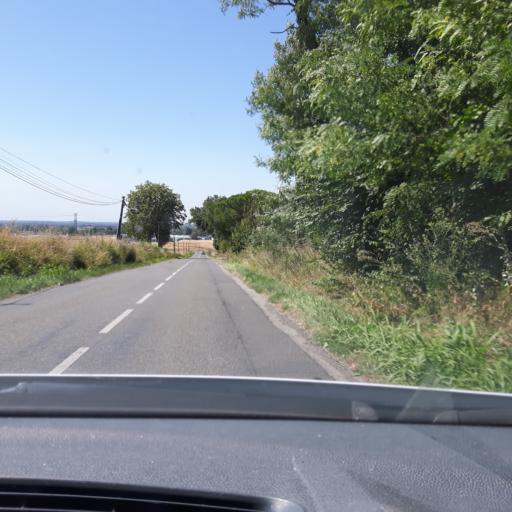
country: FR
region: Midi-Pyrenees
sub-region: Departement de la Haute-Garonne
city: Bouloc
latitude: 43.7727
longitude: 1.3903
